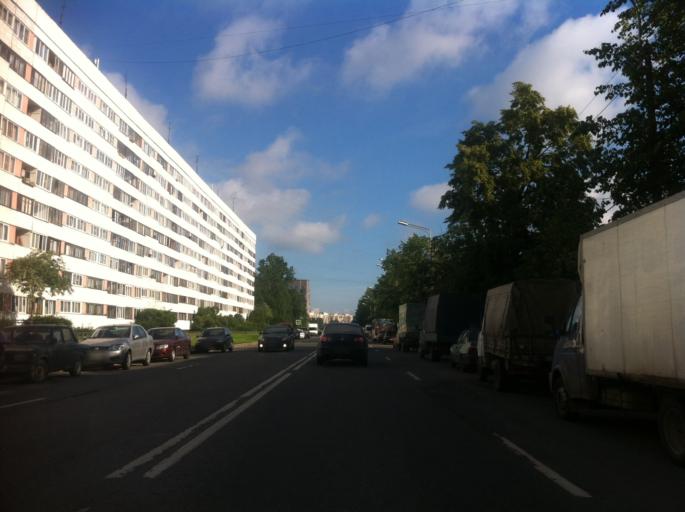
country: RU
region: St.-Petersburg
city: Dachnoye
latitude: 59.8299
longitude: 30.2208
